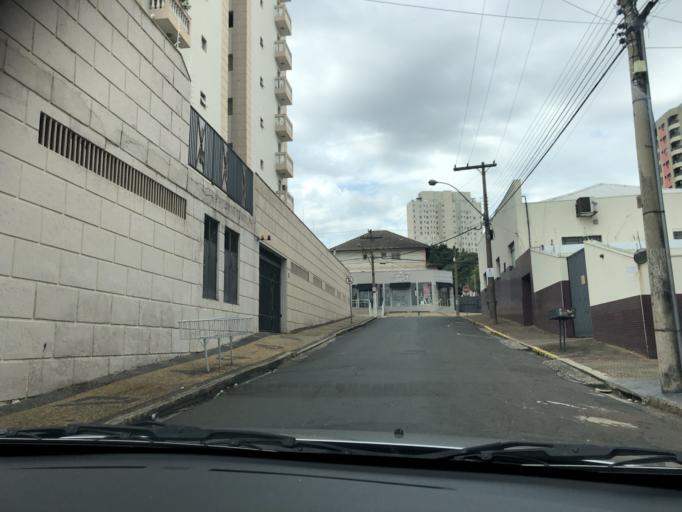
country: BR
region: Sao Paulo
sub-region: Americana
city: Americana
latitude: -22.7386
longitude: -47.3350
